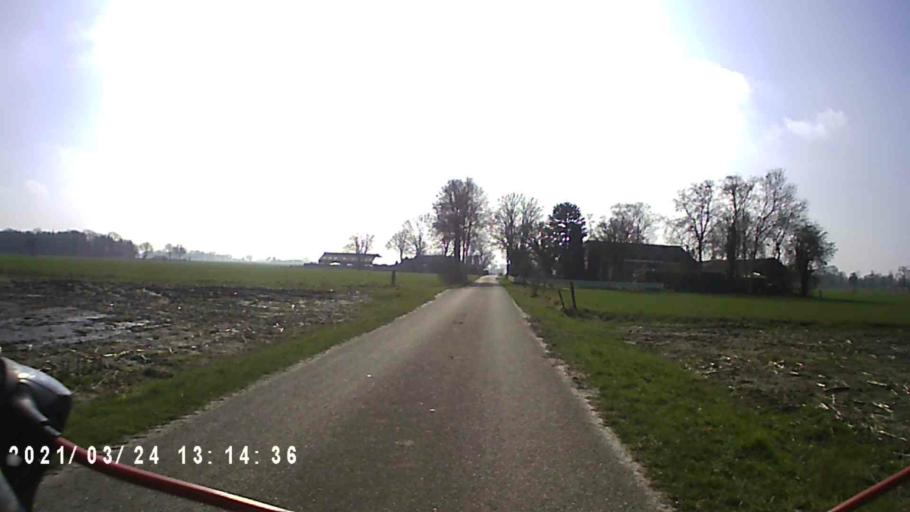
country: NL
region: Groningen
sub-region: Gemeente Leek
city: Leek
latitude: 53.1164
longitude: 6.2927
